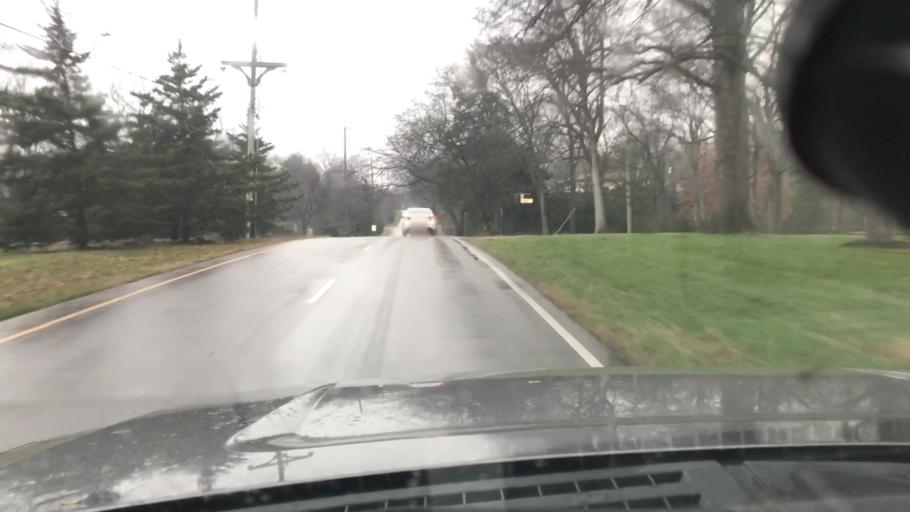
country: US
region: Tennessee
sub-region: Davidson County
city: Belle Meade
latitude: 36.0966
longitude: -86.8567
